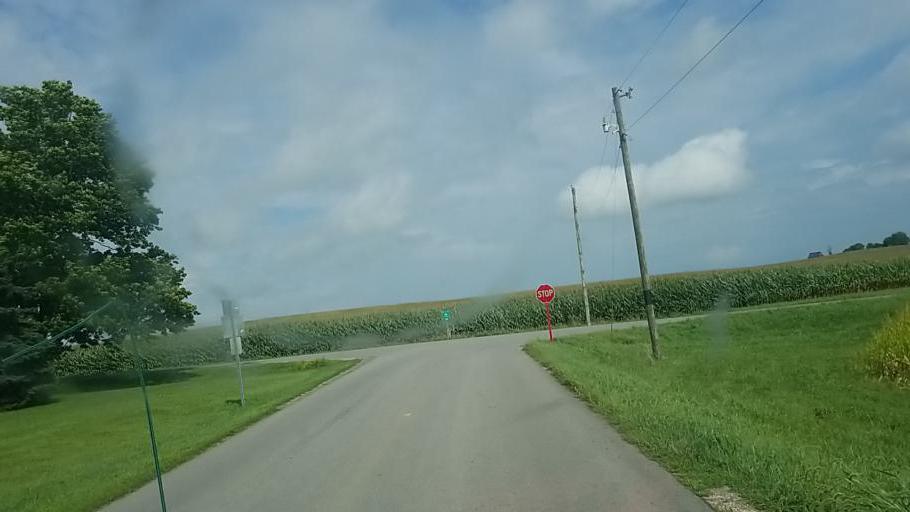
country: US
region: Ohio
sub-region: Champaign County
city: North Lewisburg
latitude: 40.2402
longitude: -83.6472
